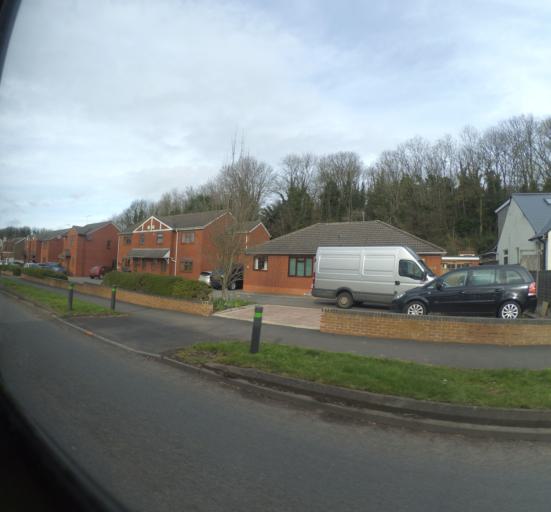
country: GB
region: England
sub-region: Warwickshire
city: Rugby
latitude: 52.3863
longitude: -1.2752
